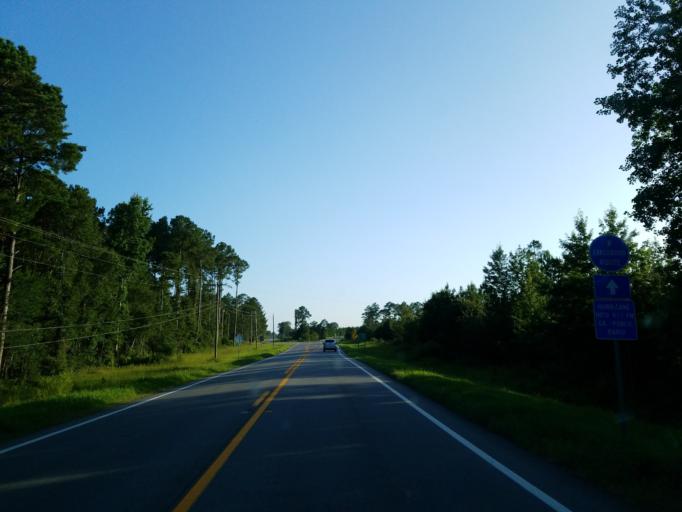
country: US
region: Georgia
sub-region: Irwin County
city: Ocilla
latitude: 31.6298
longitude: -83.4195
